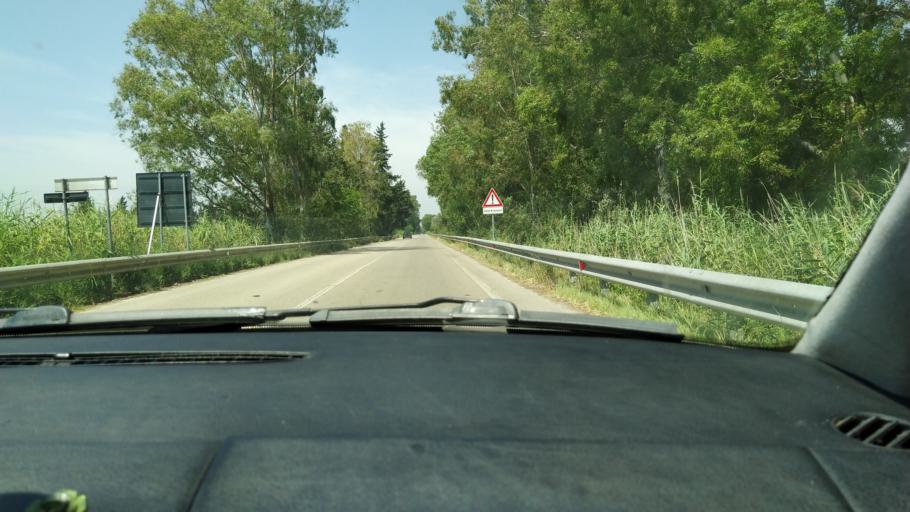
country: IT
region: Apulia
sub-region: Provincia di Taranto
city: Marina di Ginosa
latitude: 40.3718
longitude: 16.8074
